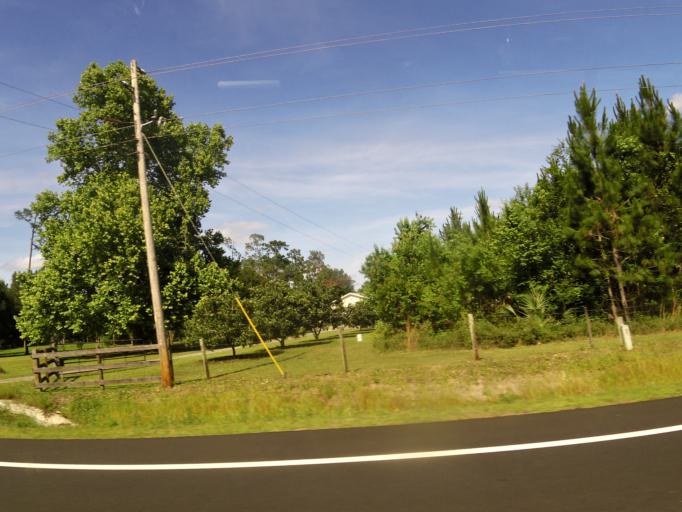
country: US
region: Florida
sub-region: Nassau County
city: Hilliard
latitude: 30.6383
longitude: -81.9018
